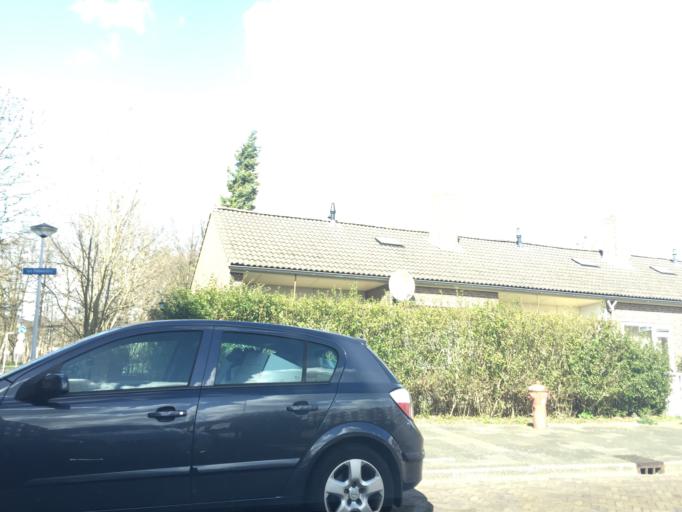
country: NL
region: South Holland
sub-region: Gemeente Leiden
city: Leiden
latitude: 52.1689
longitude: 4.5075
